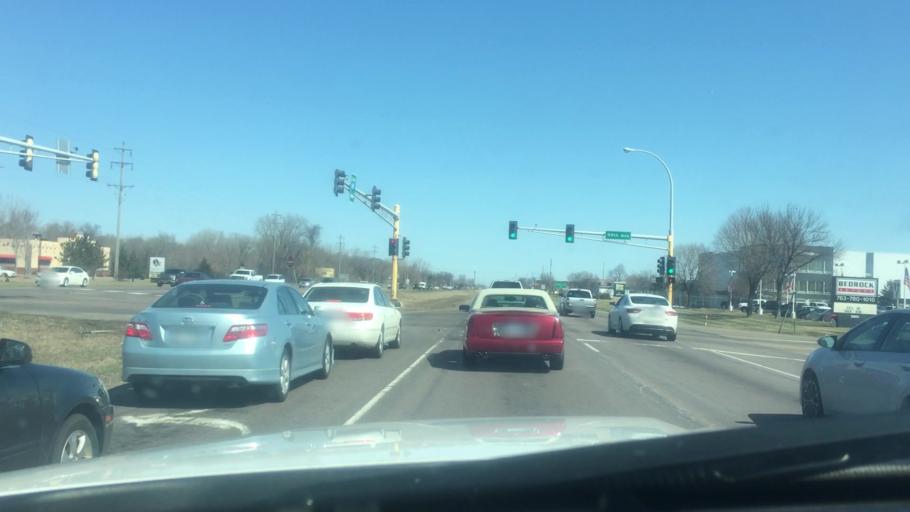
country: US
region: Minnesota
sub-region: Anoka County
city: Blaine
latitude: 45.1496
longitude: -93.2351
